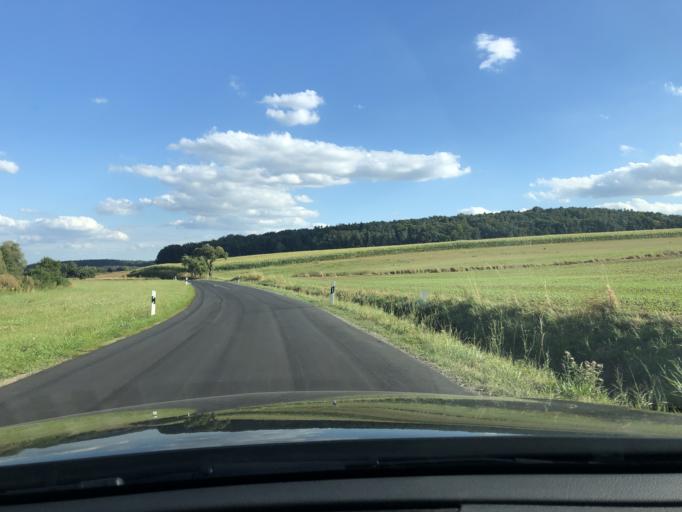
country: DE
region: Bavaria
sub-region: Regierungsbezirk Unterfranken
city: Kirchlauter
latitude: 50.0577
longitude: 10.6860
